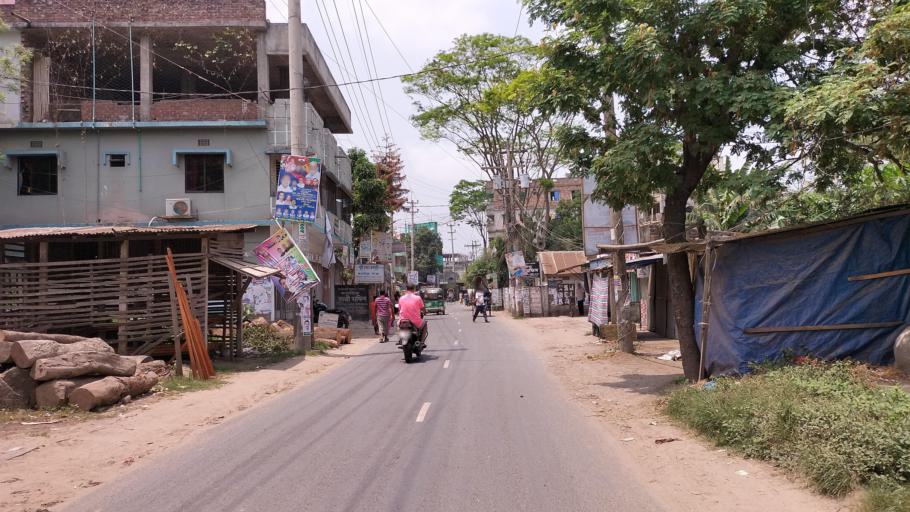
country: BD
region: Dhaka
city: Azimpur
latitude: 23.7304
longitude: 90.2779
